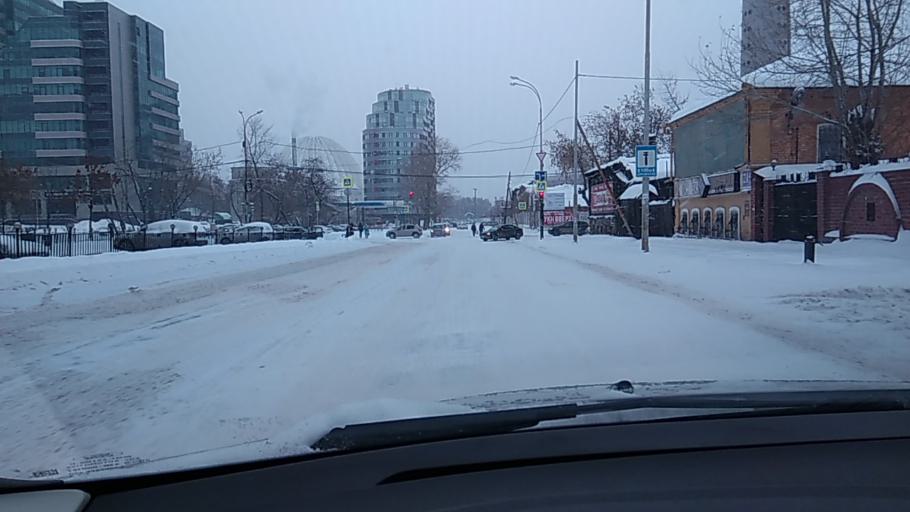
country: RU
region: Sverdlovsk
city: Yekaterinburg
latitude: 56.8223
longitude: 60.6080
